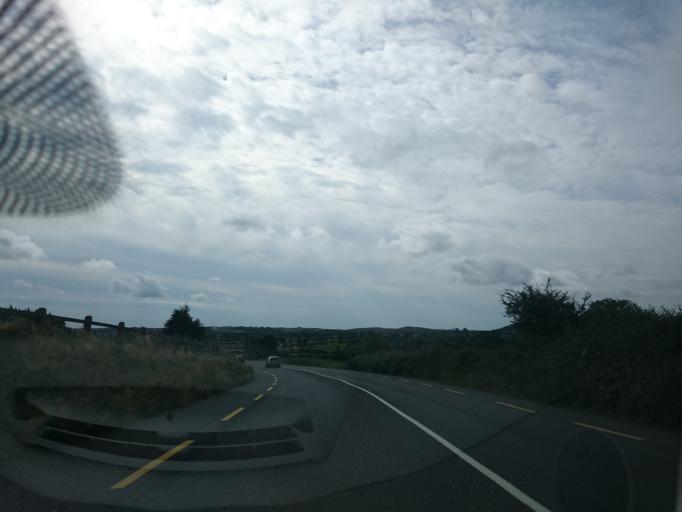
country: IE
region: Munster
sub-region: Waterford
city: Tra Mhor
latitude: 52.2007
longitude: -7.1946
